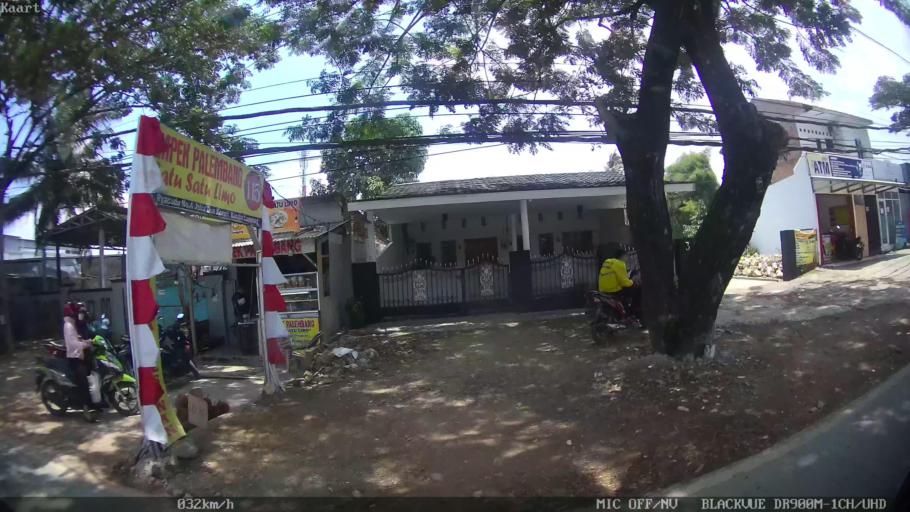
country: ID
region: Lampung
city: Kedaton
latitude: -5.3630
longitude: 105.3028
